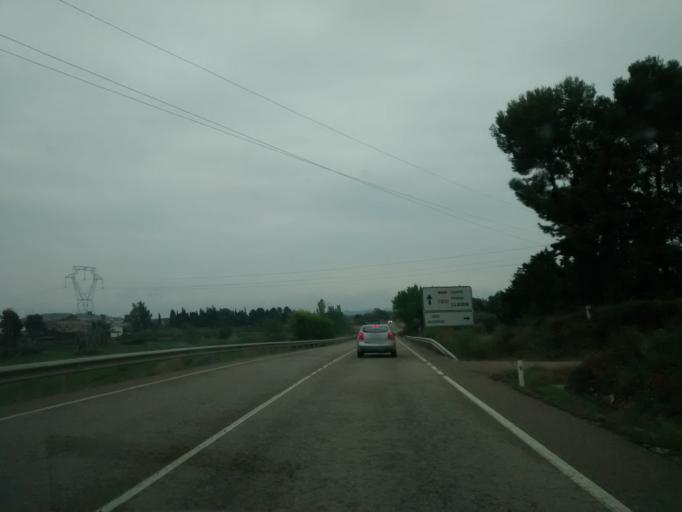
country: ES
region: Aragon
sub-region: Provincia de Zaragoza
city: Caspe
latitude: 41.2425
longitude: -0.0629
